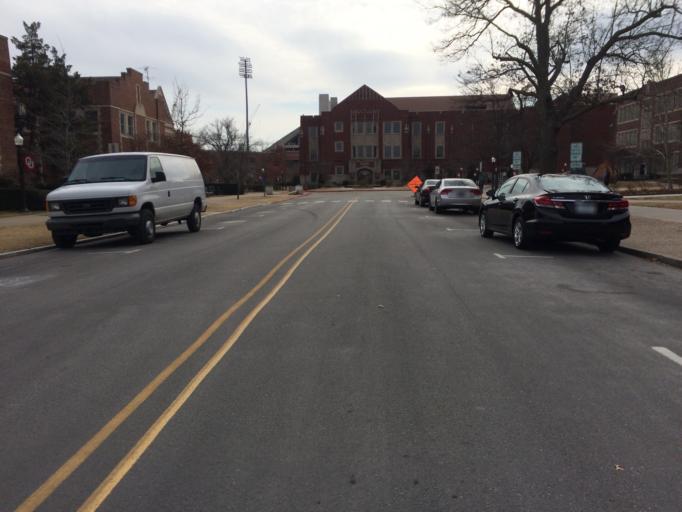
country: US
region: Oklahoma
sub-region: Cleveland County
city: Norman
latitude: 35.2093
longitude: -97.4438
